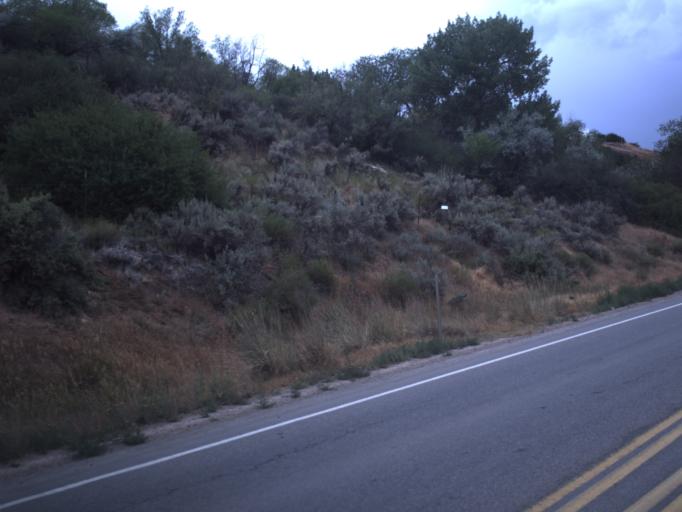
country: US
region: Utah
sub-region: Duchesne County
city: Roosevelt
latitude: 40.3108
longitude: -110.0098
